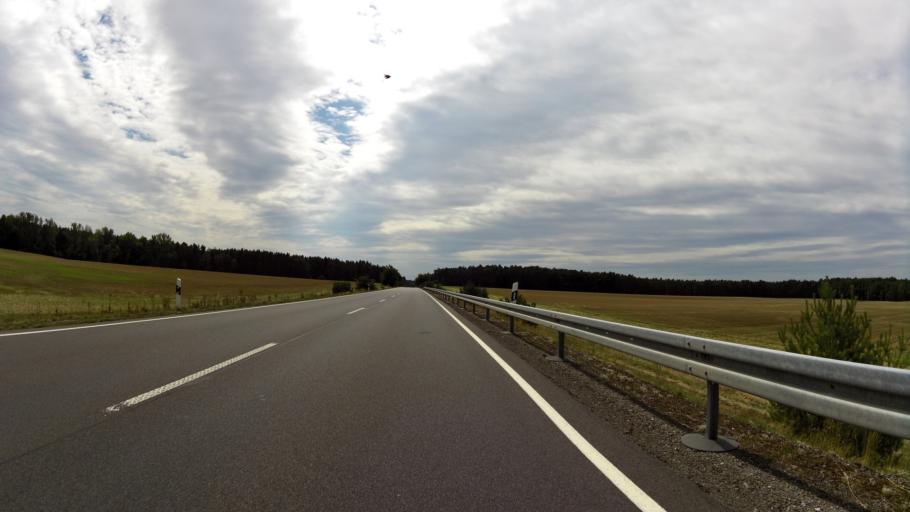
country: DE
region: Brandenburg
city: Schenkendobern
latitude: 51.9946
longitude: 14.6605
